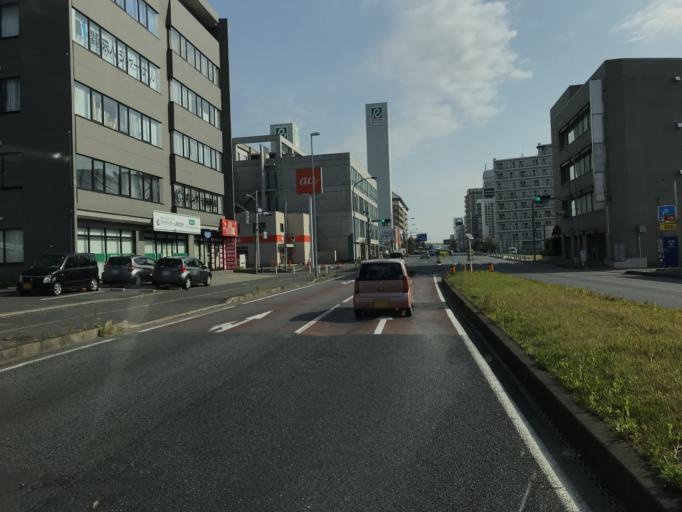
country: JP
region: Chiba
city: Narita
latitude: 35.7742
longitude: 140.3163
